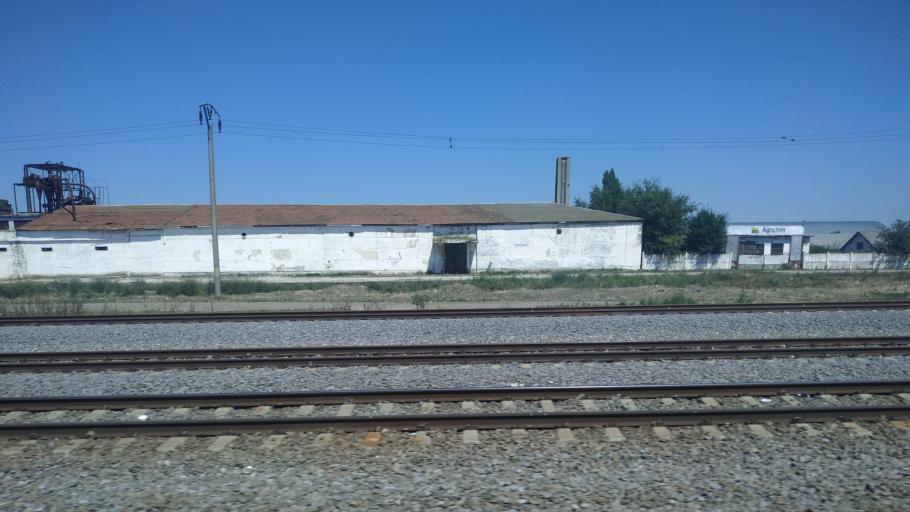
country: RO
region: Calarasi
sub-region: Comuna Borcea
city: Borcea
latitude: 44.4200
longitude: 27.7000
